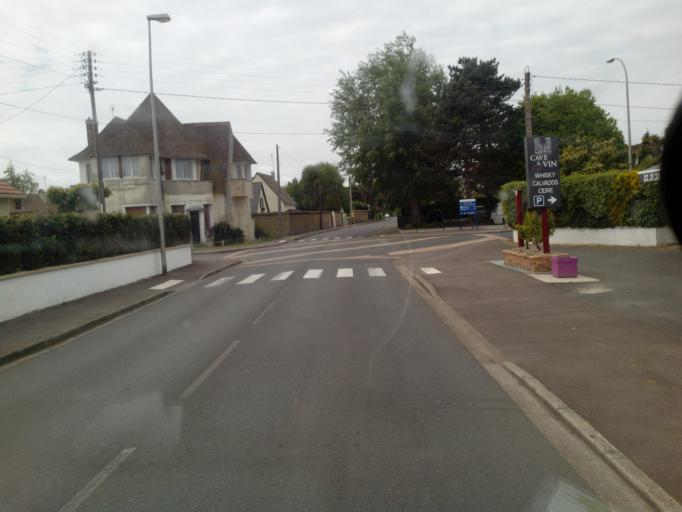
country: FR
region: Lower Normandy
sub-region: Departement du Calvados
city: Merville-Franceville-Plage
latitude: 49.2812
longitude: -0.1968
